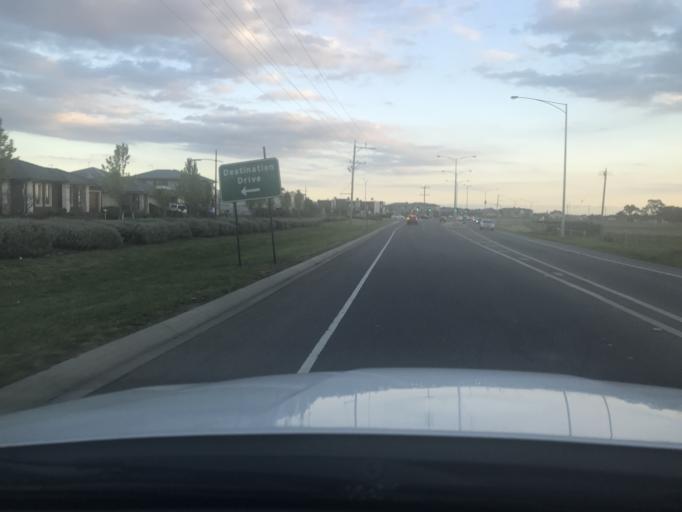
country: AU
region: Victoria
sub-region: Hume
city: Greenvale
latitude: -37.6128
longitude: 144.8854
